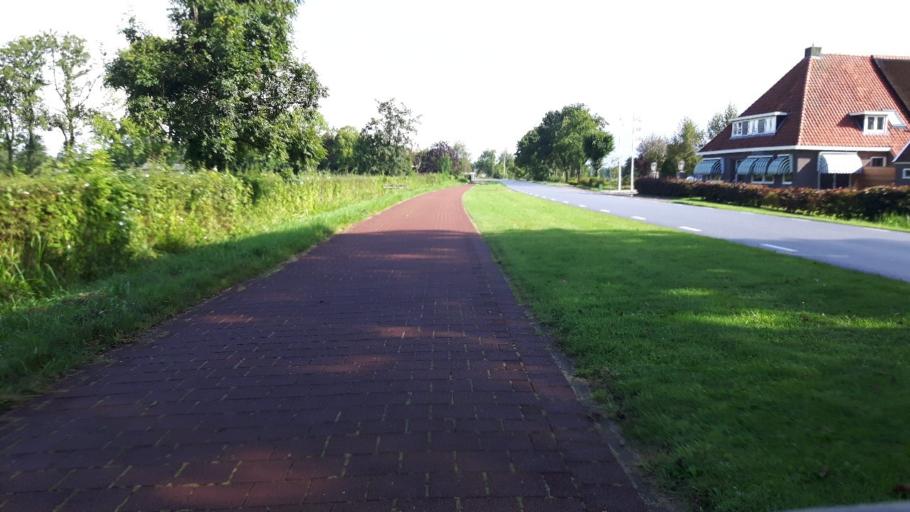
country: NL
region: Friesland
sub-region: Gemeente Smallingerland
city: Drachten
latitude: 53.0789
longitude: 6.0989
